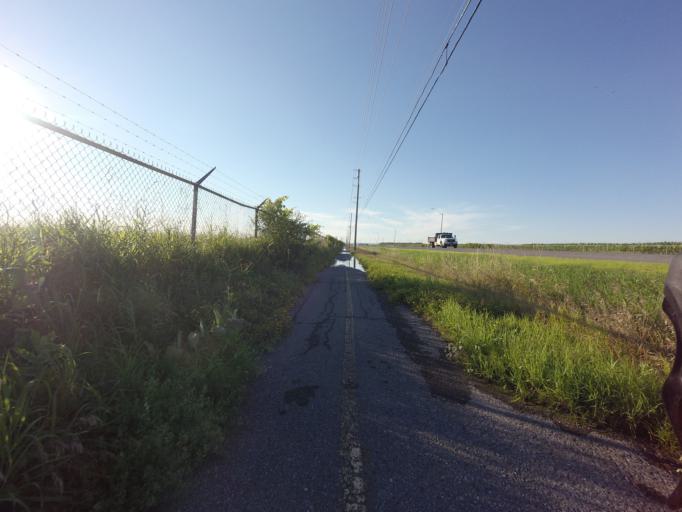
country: CA
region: Ontario
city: Bells Corners
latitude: 45.3017
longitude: -75.7653
